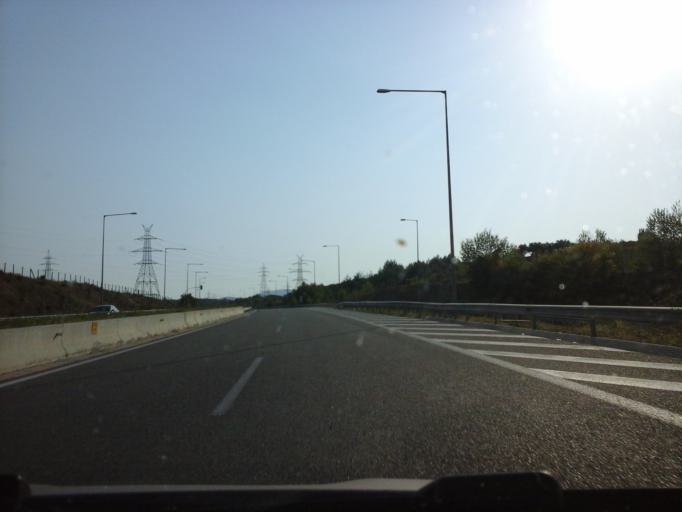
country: GR
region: East Macedonia and Thrace
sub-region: Nomos Xanthis
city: Petrochori
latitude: 41.0686
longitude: 24.7514
